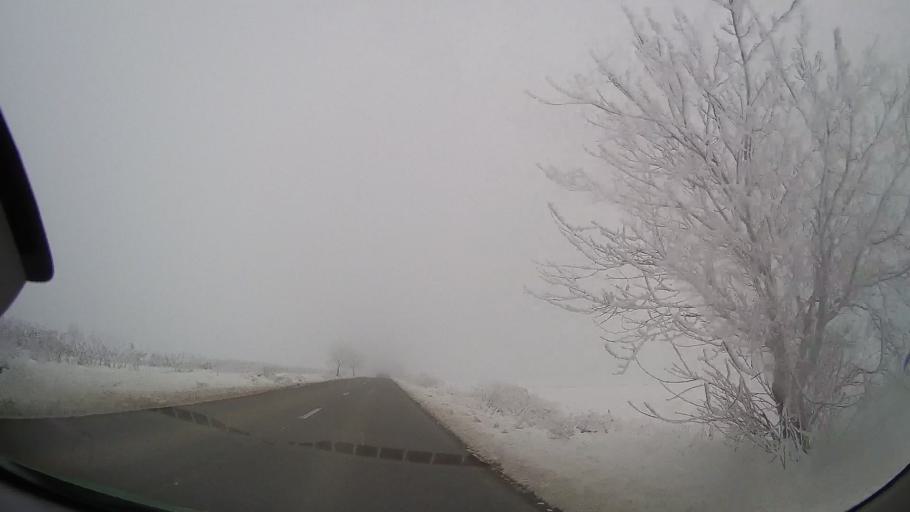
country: RO
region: Iasi
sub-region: Comuna Mogosesti-Siret
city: Mogosesti-Siret
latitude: 47.1511
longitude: 26.7775
